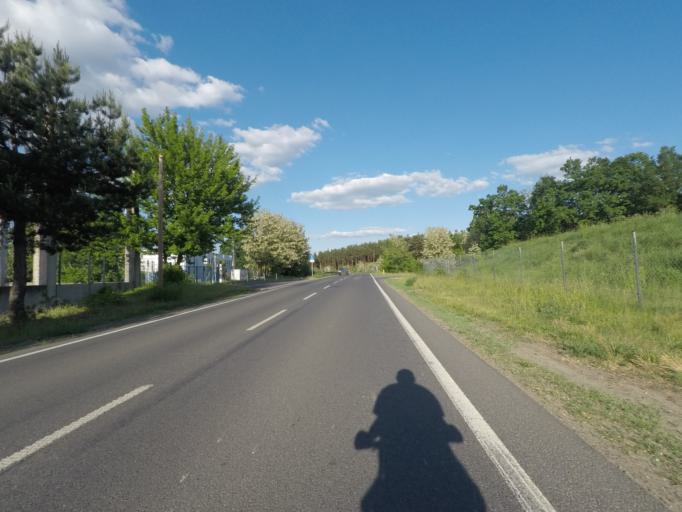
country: DE
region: Brandenburg
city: Eberswalde
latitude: 52.8513
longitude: 13.7946
